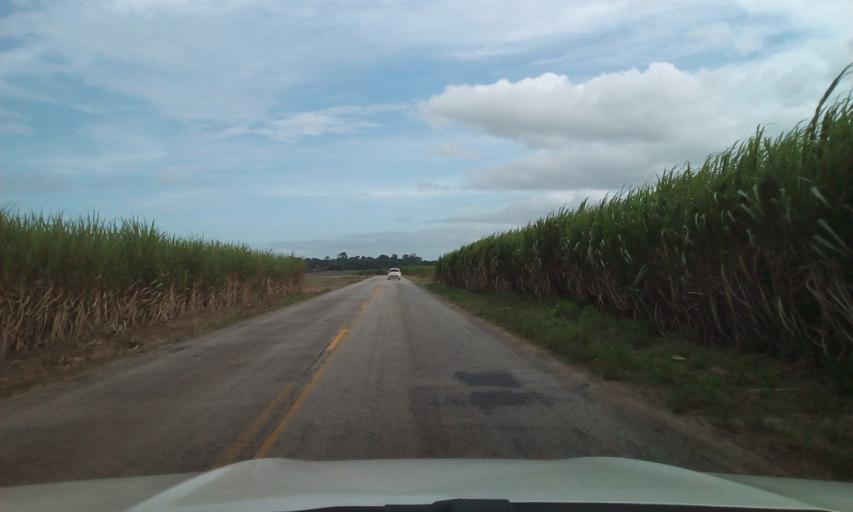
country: BR
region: Paraiba
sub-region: Santa Rita
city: Santa Rita
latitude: -7.0670
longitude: -34.9885
